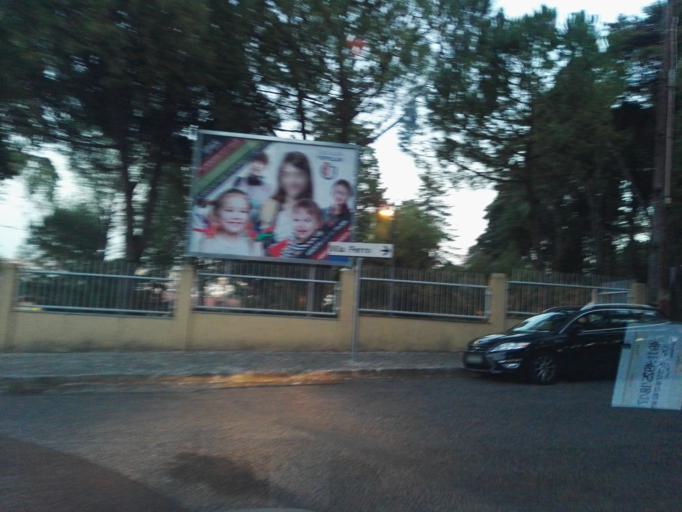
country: PT
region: Lisbon
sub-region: Odivelas
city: Pontinha
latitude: 38.7311
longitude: -9.1753
